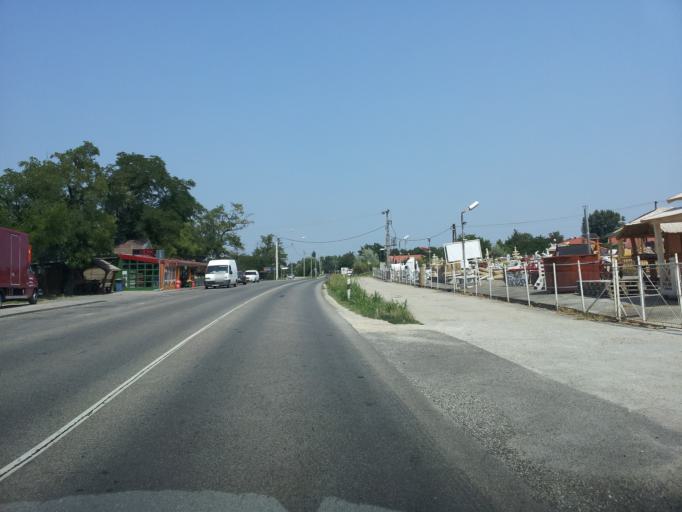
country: HU
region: Pest
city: Dunavarsany
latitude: 47.2900
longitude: 19.0296
